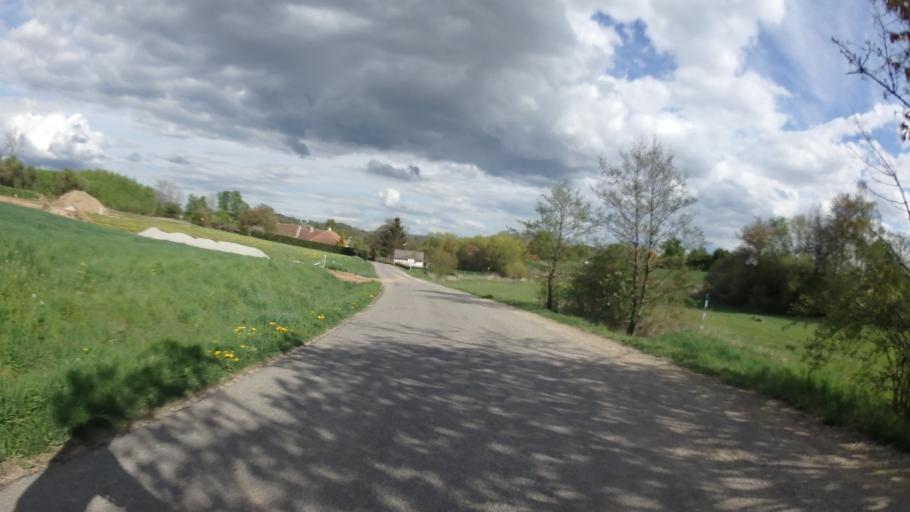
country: CZ
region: Vysocina
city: Merin
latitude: 49.3394
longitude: 15.8959
